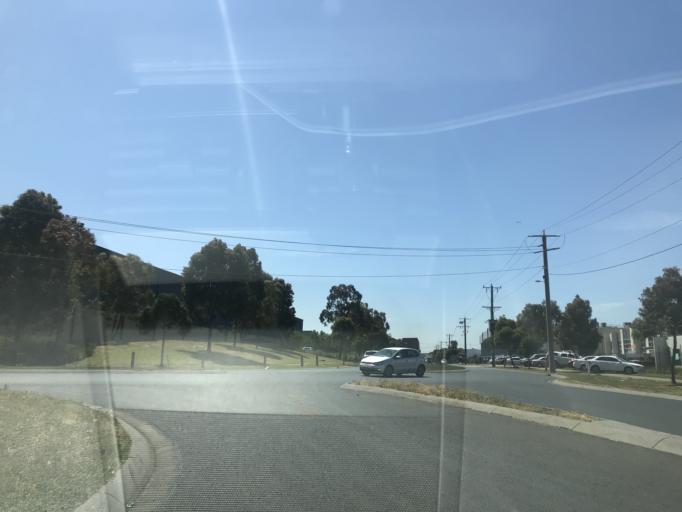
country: AU
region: Victoria
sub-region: Brimbank
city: Derrimut
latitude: -37.8172
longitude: 144.7820
